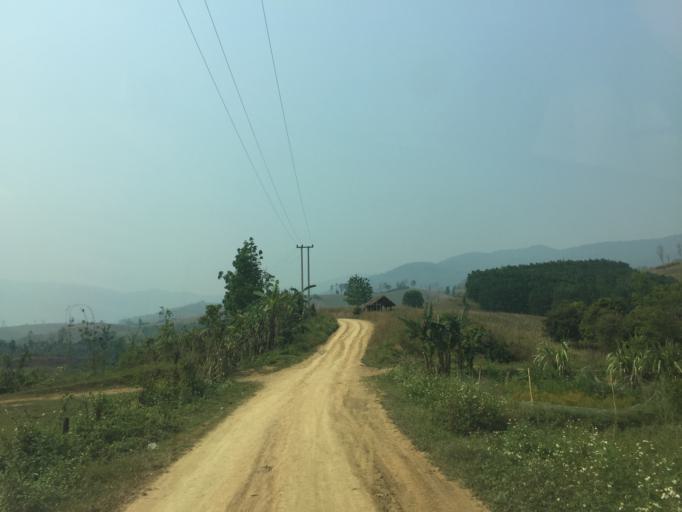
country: TH
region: Phayao
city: Phu Sang
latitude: 19.5935
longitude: 100.5280
